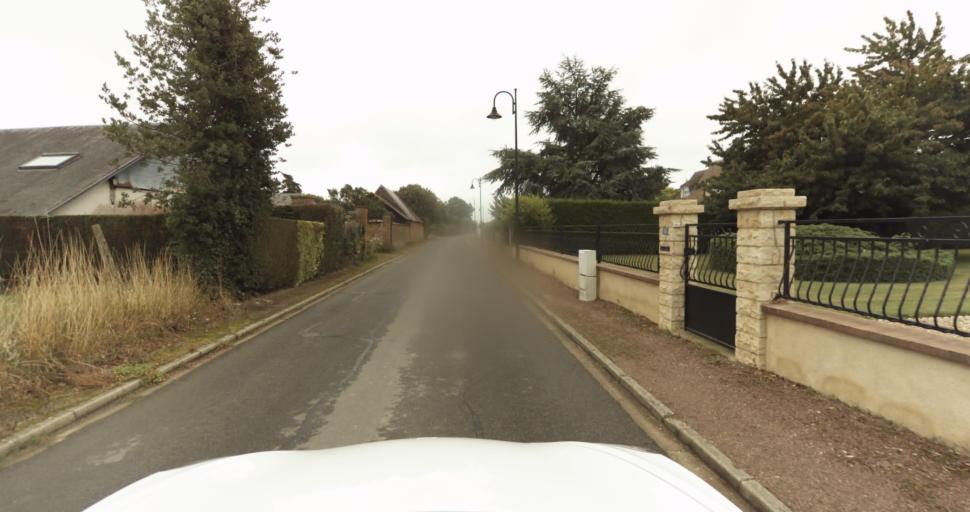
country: FR
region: Haute-Normandie
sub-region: Departement de l'Eure
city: Aviron
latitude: 49.0751
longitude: 1.0906
